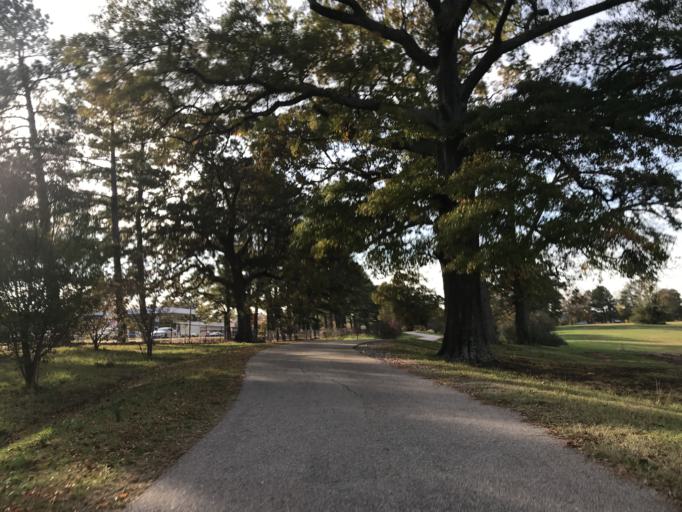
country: US
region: North Carolina
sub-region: Wake County
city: West Raleigh
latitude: 35.7942
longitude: -78.6858
